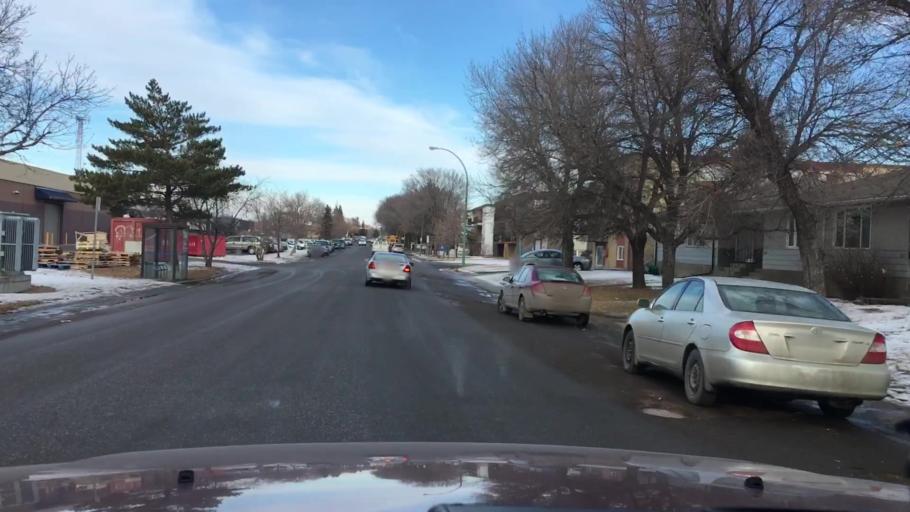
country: CA
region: Saskatchewan
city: Regina
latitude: 50.4813
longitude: -104.6137
